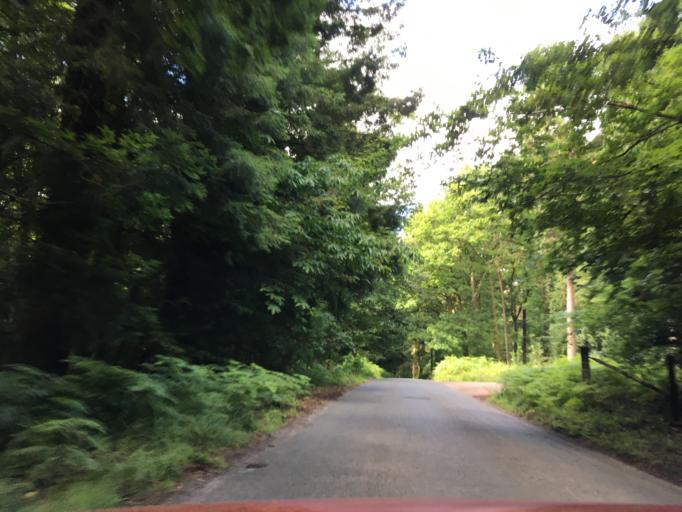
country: GB
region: England
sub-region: Gloucestershire
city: Cinderford
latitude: 51.7962
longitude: -2.4947
